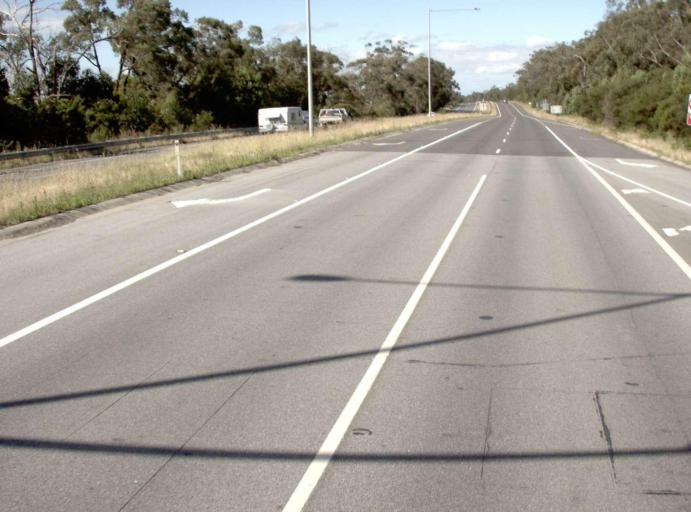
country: AU
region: Victoria
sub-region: Cardinia
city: Koo-Wee-Rup
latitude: -38.3792
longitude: 145.5560
